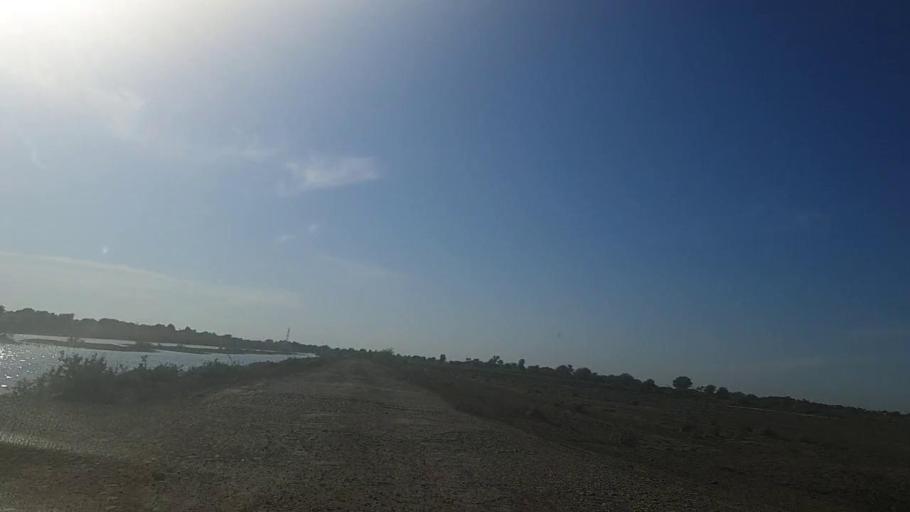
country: PK
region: Sindh
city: Pithoro
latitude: 25.5110
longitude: 69.3984
